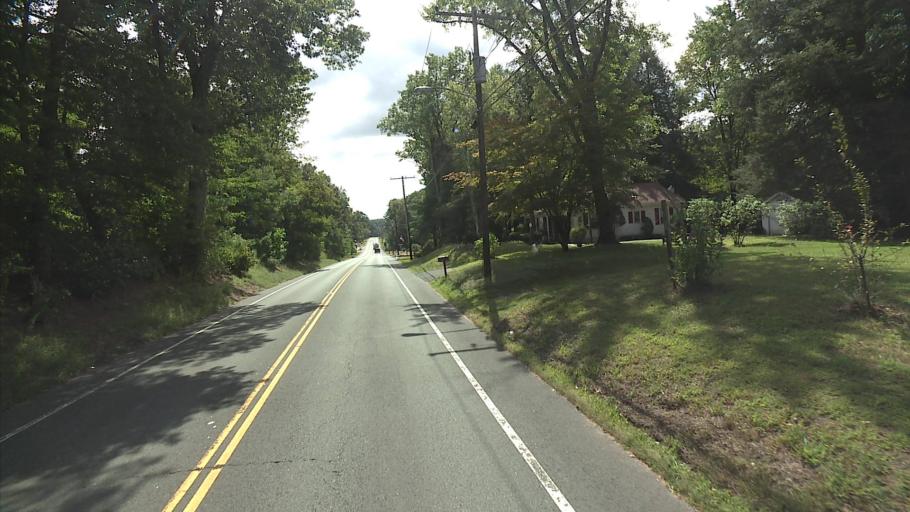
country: US
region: Connecticut
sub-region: Hartford County
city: Tariffville
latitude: 41.9367
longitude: -72.7716
